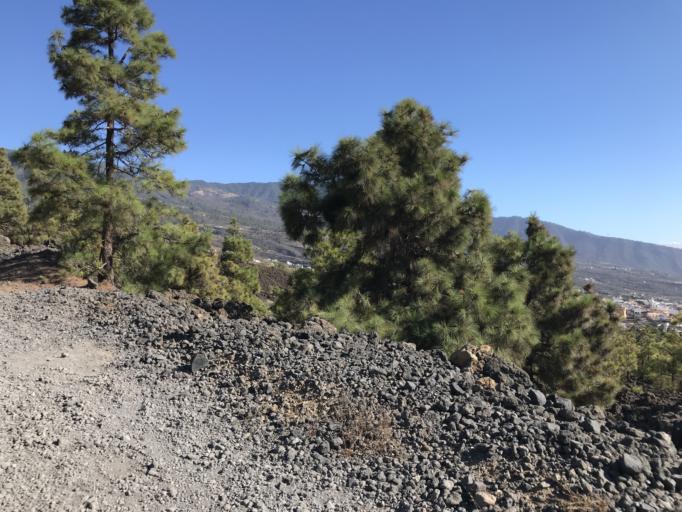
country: ES
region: Canary Islands
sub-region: Provincia de Santa Cruz de Tenerife
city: Arafo
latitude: 28.3302
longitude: -16.4255
